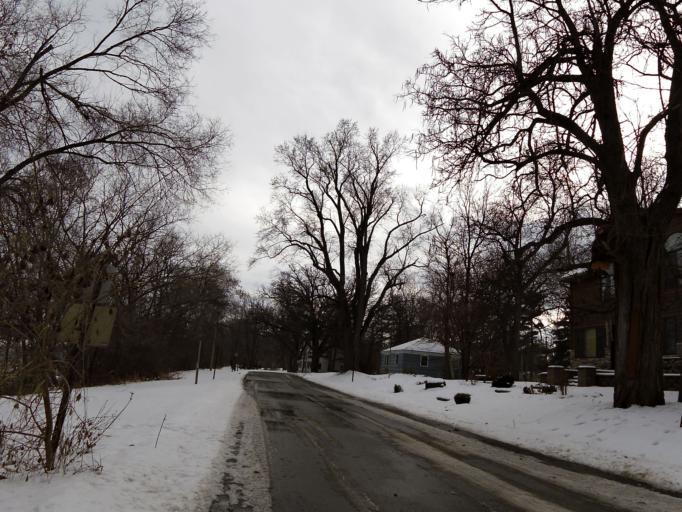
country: US
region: Minnesota
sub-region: Washington County
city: Lakeland
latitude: 44.9618
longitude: -92.7671
